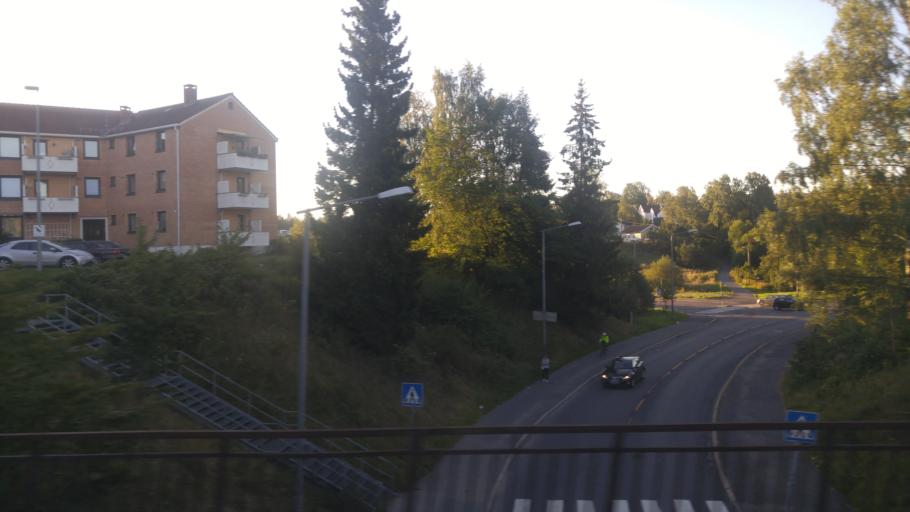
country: NO
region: Akershus
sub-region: Lorenskog
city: Kjenn
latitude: 59.9502
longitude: 10.8880
